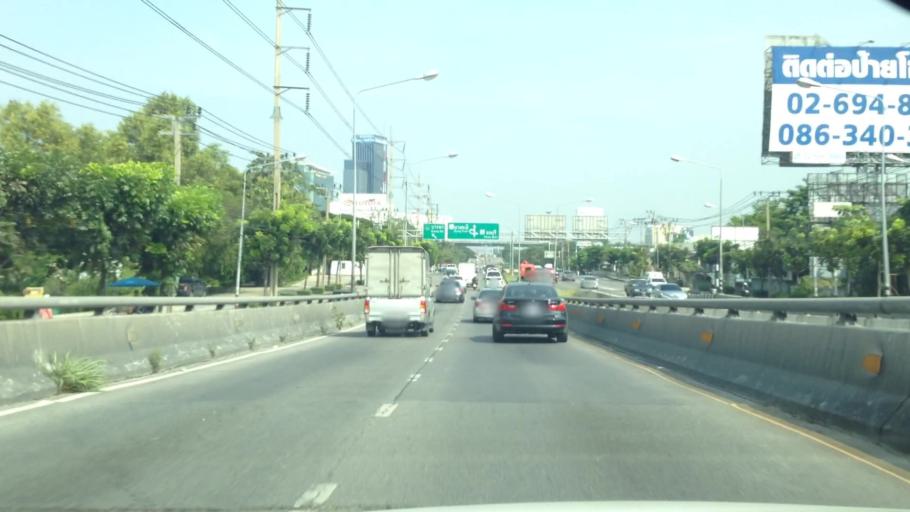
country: TH
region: Bangkok
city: Bang Na
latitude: 13.6585
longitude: 100.6428
